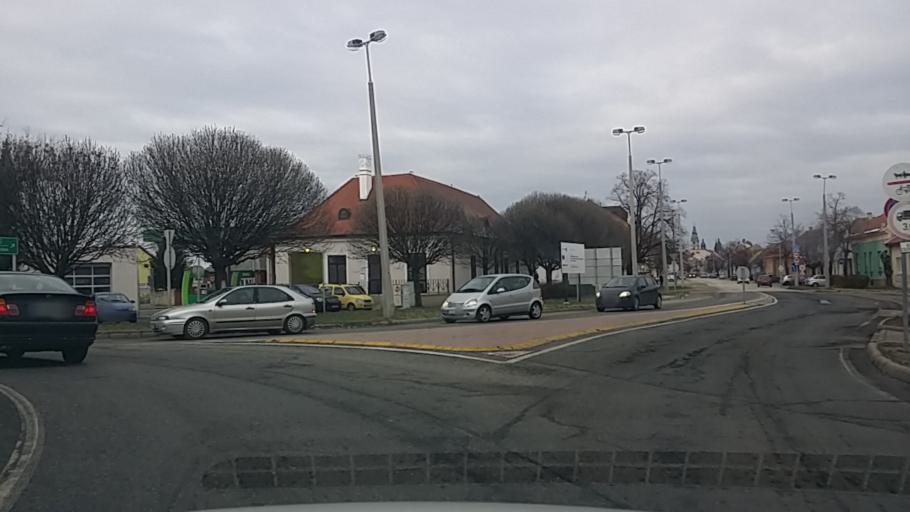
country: HU
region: Veszprem
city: Papa
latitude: 47.3220
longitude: 17.4766
